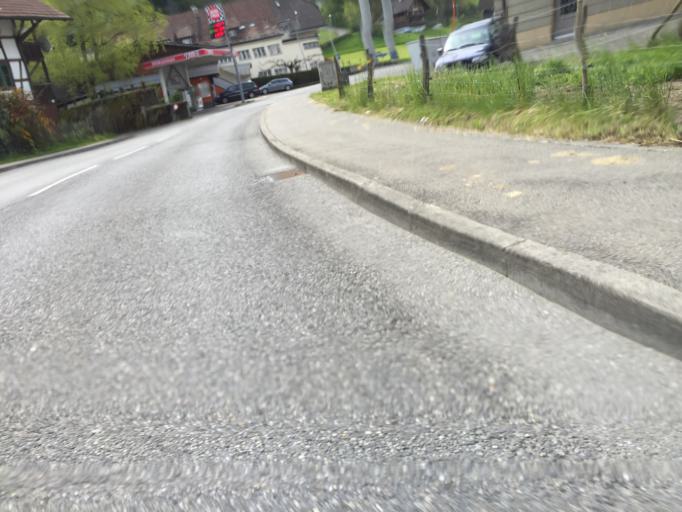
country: CH
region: Fribourg
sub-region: Sense District
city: Flamatt
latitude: 46.8901
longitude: 7.3095
